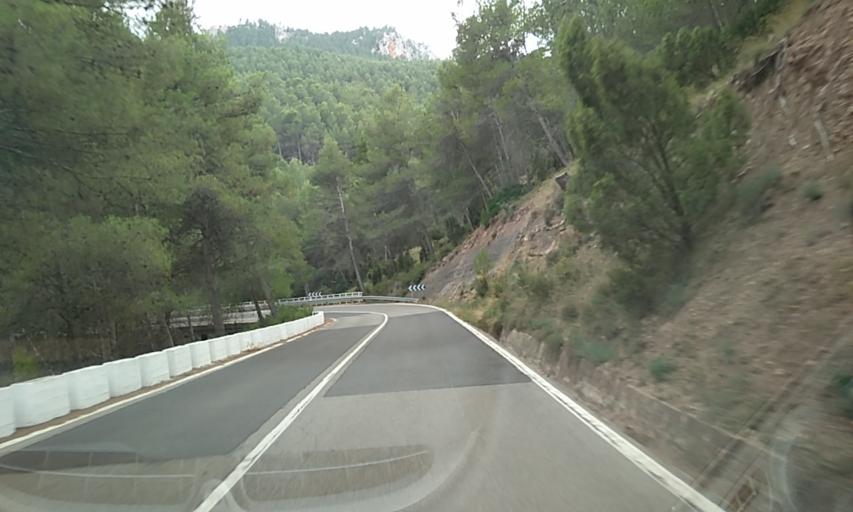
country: ES
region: Valencia
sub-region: Provincia de Castello
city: Puebla de Arenoso
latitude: 40.0880
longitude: -0.5579
